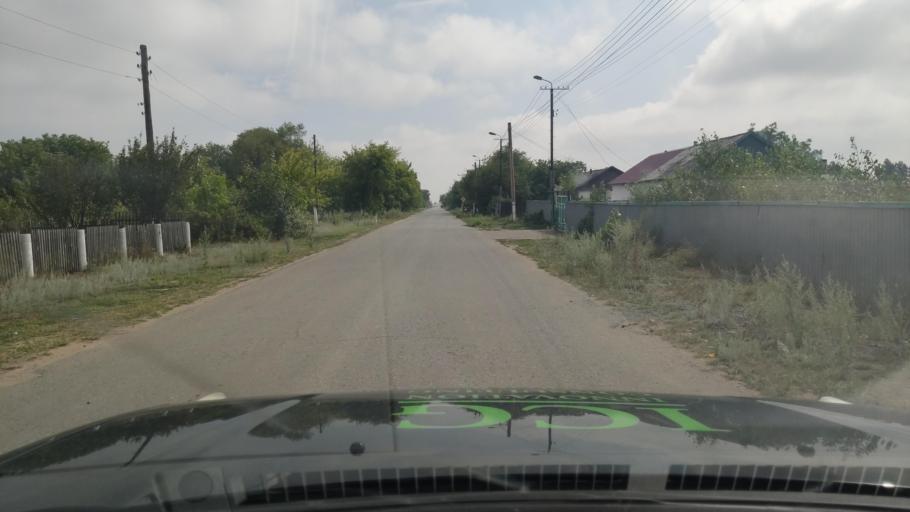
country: KZ
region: Pavlodar
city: Koktobe
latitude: 51.9650
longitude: 77.6339
